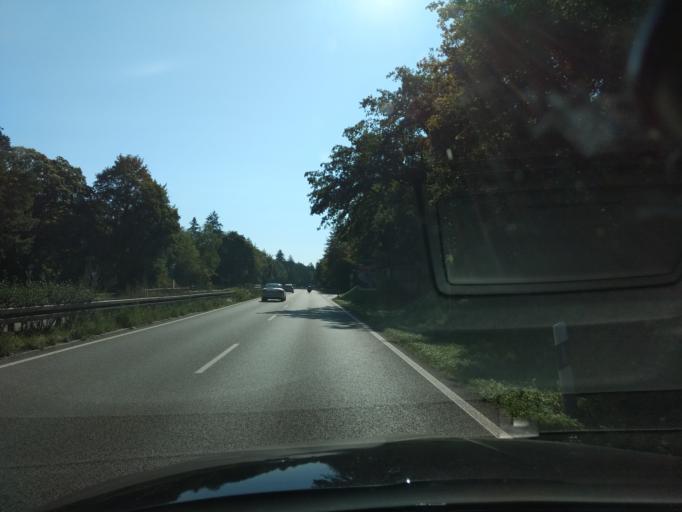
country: DE
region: Bavaria
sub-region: Upper Bavaria
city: Wolfratshausen
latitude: 47.8903
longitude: 11.4472
